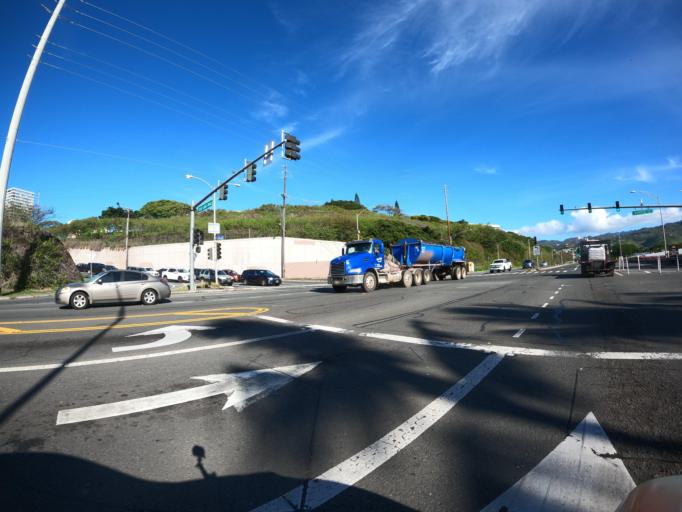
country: US
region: Hawaii
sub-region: Honolulu County
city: Halawa Heights
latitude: 21.3448
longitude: -157.8992
